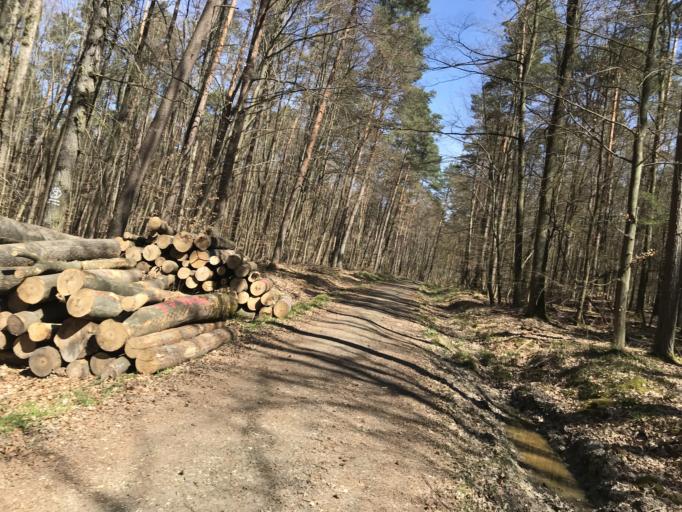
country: DE
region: Hesse
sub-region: Regierungsbezirk Giessen
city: Alten Buseck
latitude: 50.6432
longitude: 8.7557
